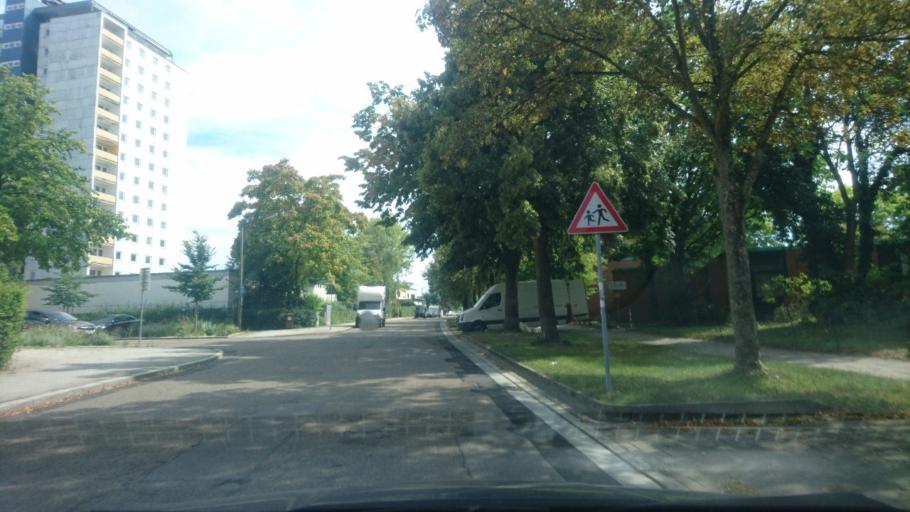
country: DE
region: Bavaria
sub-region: Upper Palatinate
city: Sinzing
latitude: 49.0194
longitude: 12.0475
